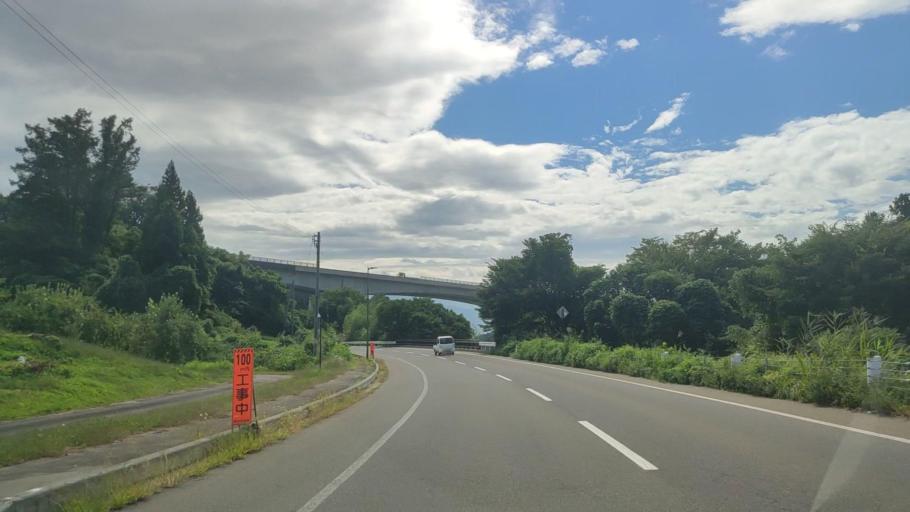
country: JP
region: Nagano
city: Nakano
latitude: 36.7871
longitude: 138.3181
